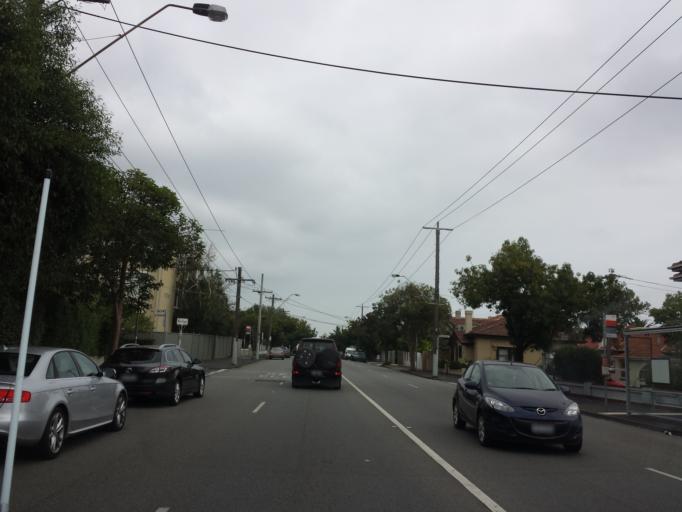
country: AU
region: Victoria
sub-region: Stonnington
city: Windsor
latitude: -37.8564
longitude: 145.0018
